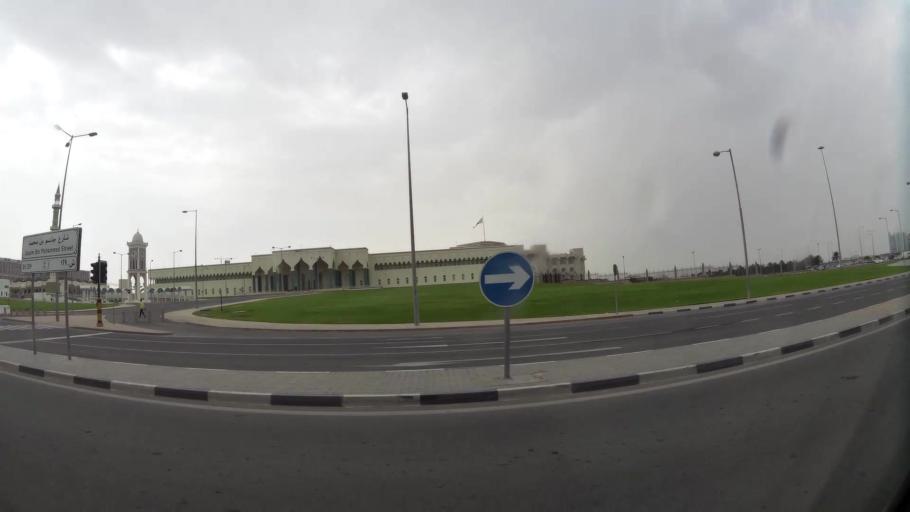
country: QA
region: Baladiyat ad Dawhah
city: Doha
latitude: 25.2908
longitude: 51.5300
